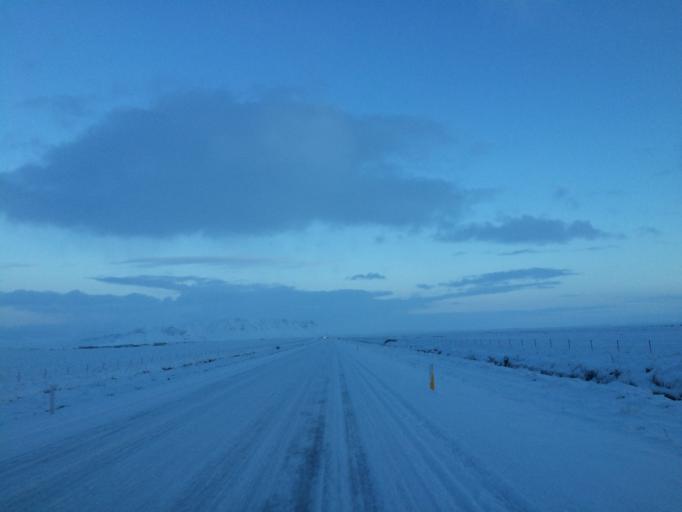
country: IS
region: South
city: Selfoss
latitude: 63.8743
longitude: -21.0946
